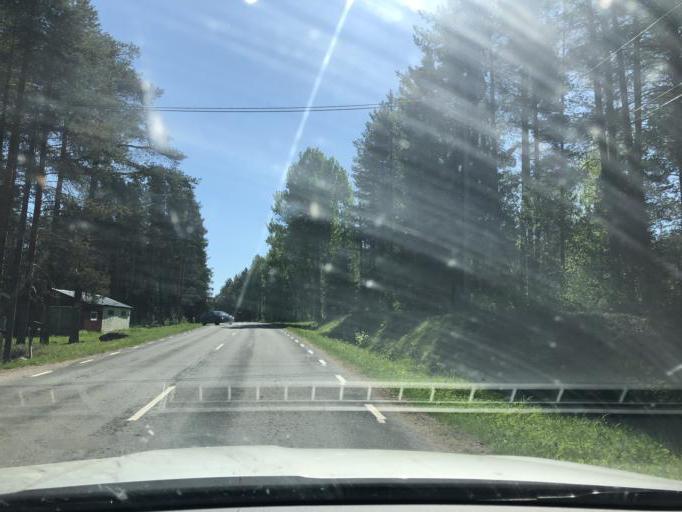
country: SE
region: Norrbotten
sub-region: Lulea Kommun
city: Sodra Sunderbyn
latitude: 65.6622
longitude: 21.9750
